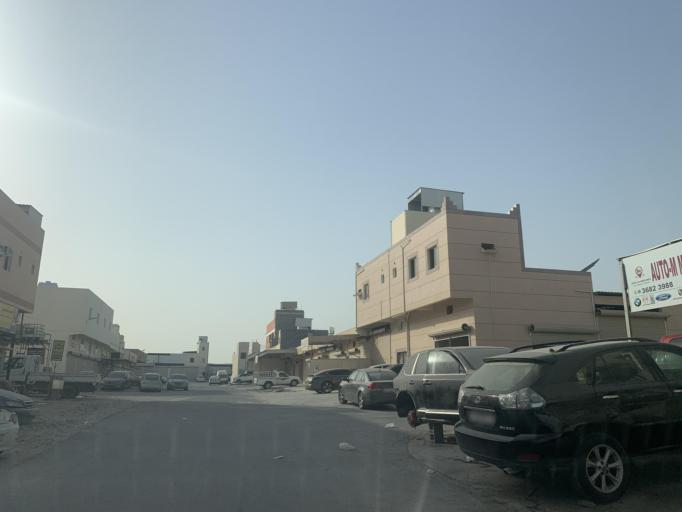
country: BH
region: Central Governorate
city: Madinat Hamad
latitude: 26.1454
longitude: 50.4845
